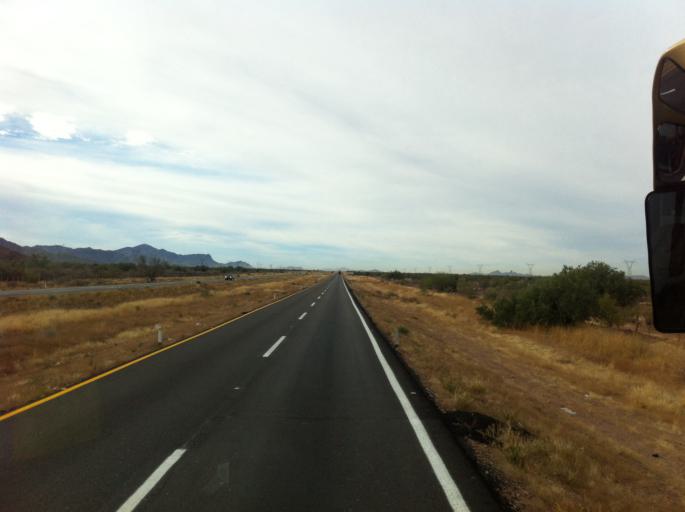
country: MX
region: Sonora
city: Hermosillo
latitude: 28.6243
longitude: -111.0135
